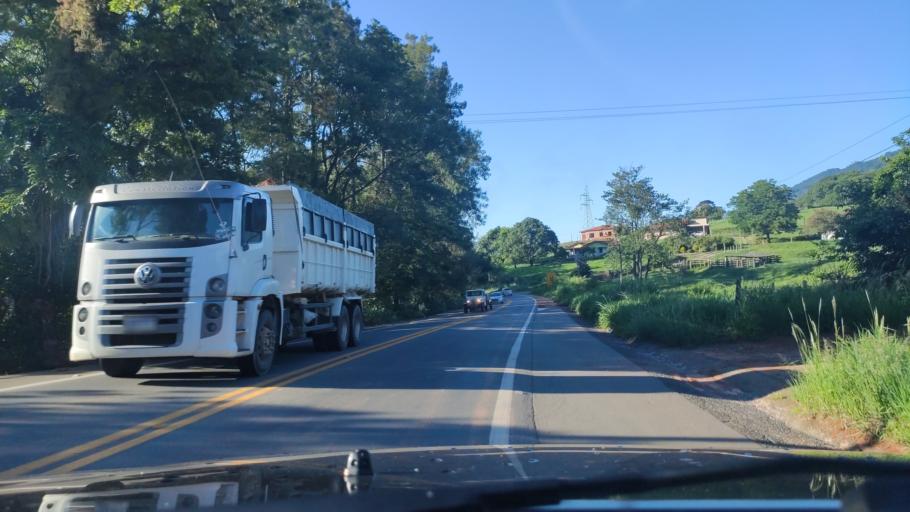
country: BR
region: Sao Paulo
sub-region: Socorro
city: Socorro
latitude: -22.5563
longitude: -46.5604
